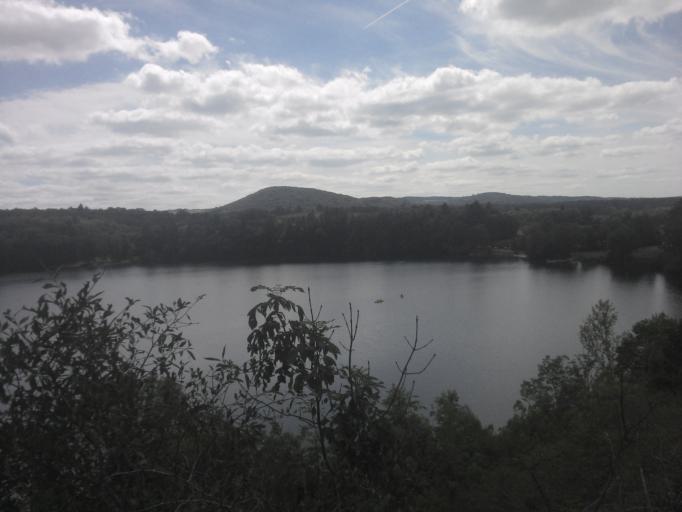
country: FR
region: Auvergne
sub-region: Departement du Puy-de-Dome
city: Manzat
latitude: 45.9840
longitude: 2.9910
